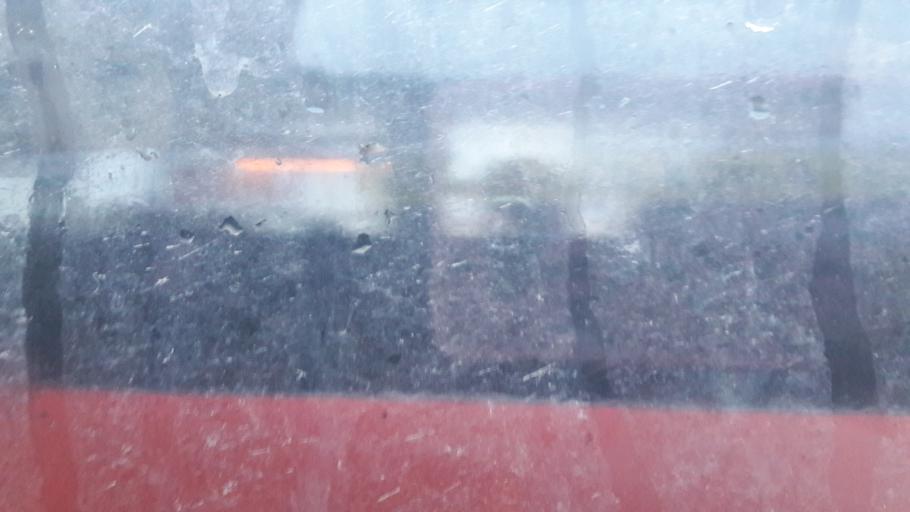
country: RU
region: Tula
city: Tula
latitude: 54.1895
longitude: 37.6138
